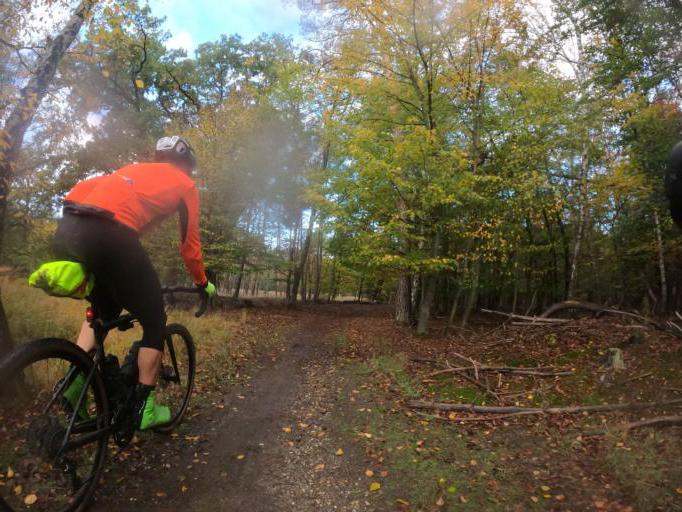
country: DE
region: Hesse
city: Raunheim
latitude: 49.9930
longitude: 8.4863
